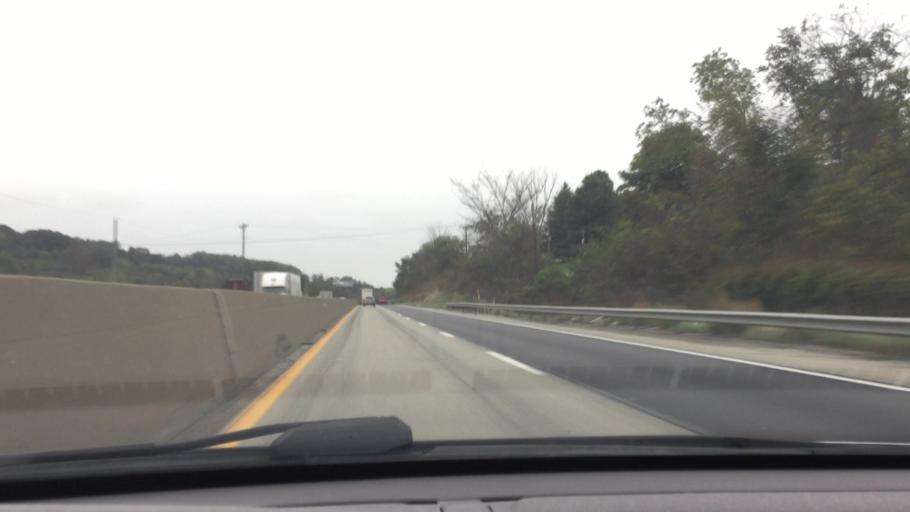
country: US
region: Pennsylvania
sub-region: Washington County
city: Bentleyville
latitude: 40.1409
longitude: -80.0203
